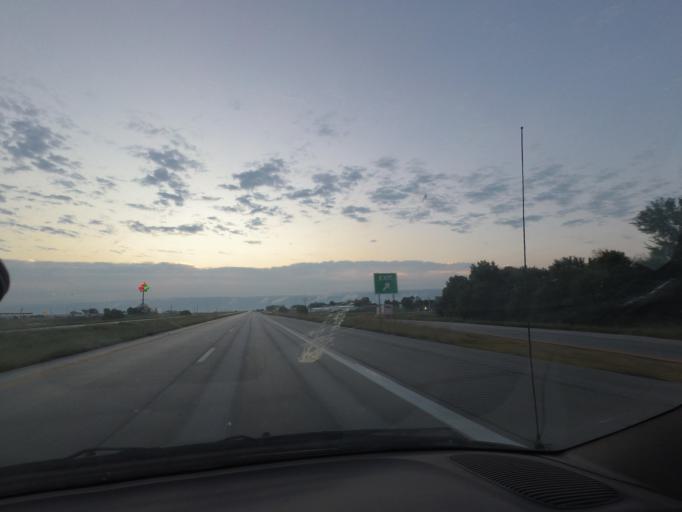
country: US
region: Missouri
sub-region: Macon County
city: Macon
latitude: 39.7603
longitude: -92.5671
